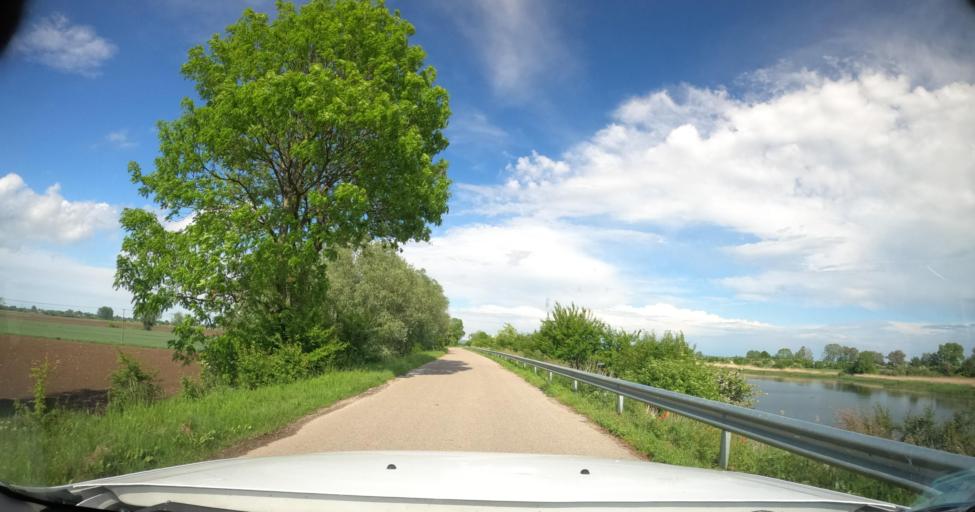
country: PL
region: Warmian-Masurian Voivodeship
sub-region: Powiat elblaski
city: Gronowo Elblaskie
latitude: 54.1792
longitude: 19.2679
